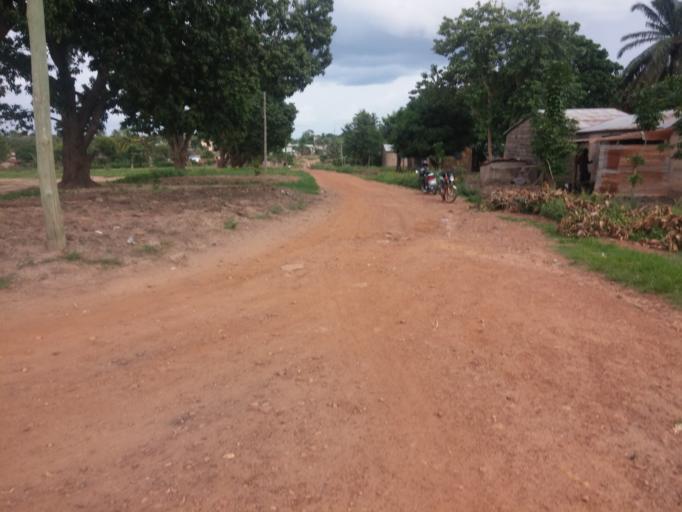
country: TG
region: Kara
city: Kara
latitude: 9.5462
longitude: 1.2055
